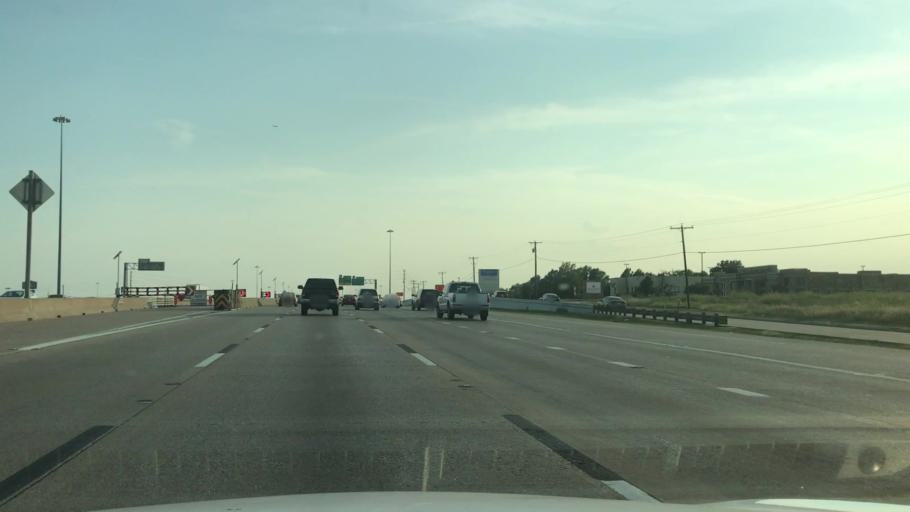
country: US
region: Texas
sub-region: Dallas County
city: Mesquite
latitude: 32.8287
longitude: -96.6194
